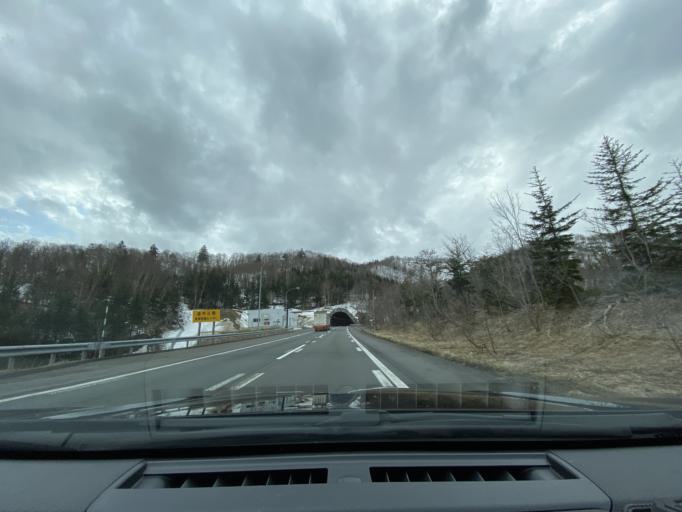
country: JP
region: Hokkaido
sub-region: Asahikawa-shi
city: Asahikawa
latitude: 43.7851
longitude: 142.2367
